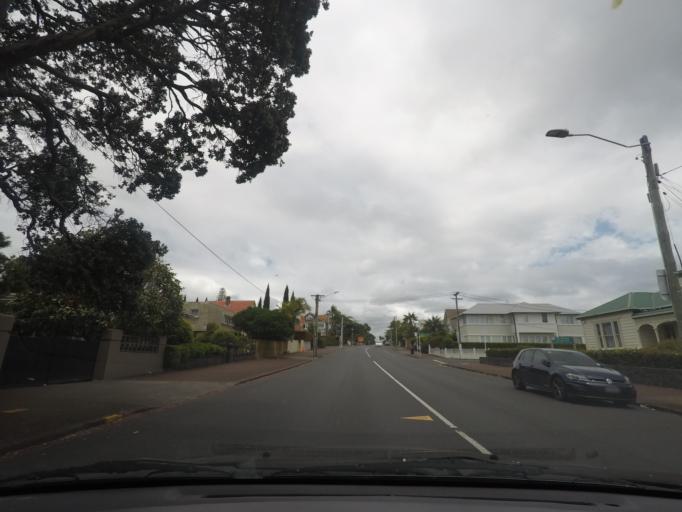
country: NZ
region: Auckland
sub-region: Auckland
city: Auckland
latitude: -36.8531
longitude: 174.7865
